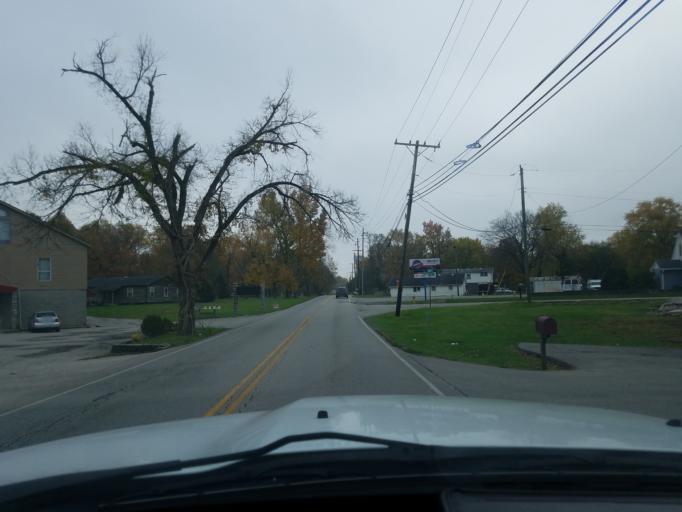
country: US
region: Indiana
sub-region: Clark County
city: Clarksville
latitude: 38.3333
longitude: -85.7941
